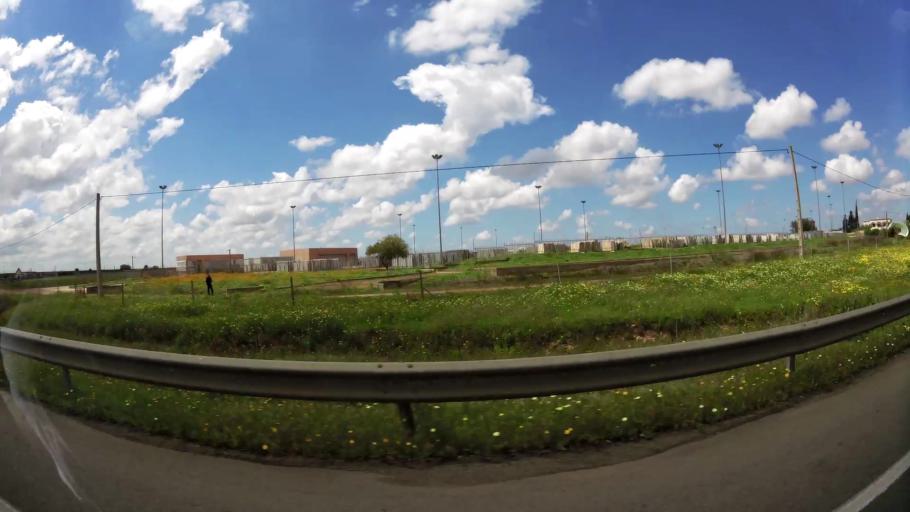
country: MA
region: Chaouia-Ouardigha
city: Nouaseur
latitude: 33.3917
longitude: -7.6206
